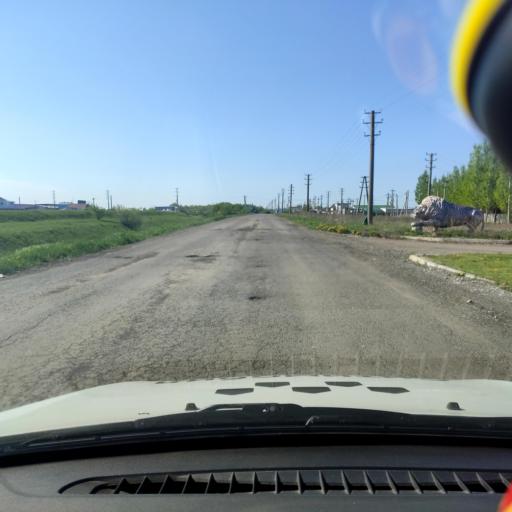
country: RU
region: Samara
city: Podstepki
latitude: 53.5263
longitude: 49.1970
